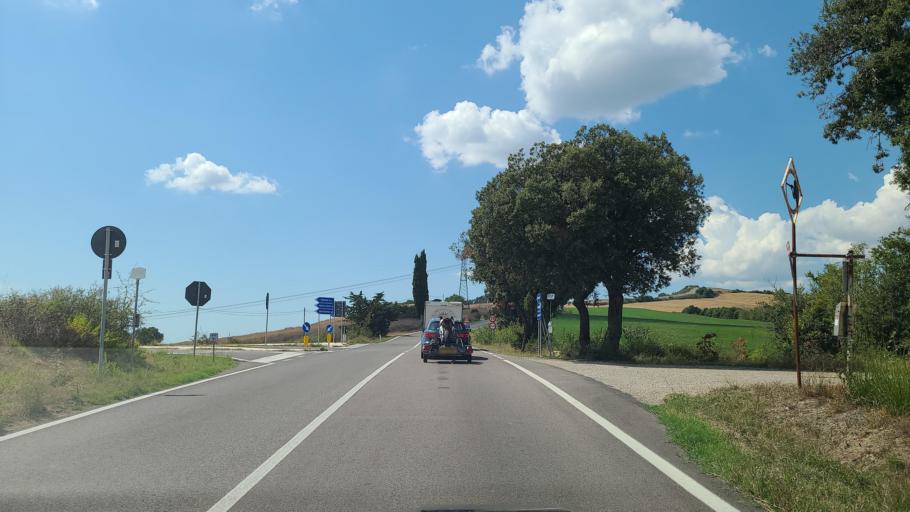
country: IT
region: Tuscany
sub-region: Provincia di Siena
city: San Gimignano
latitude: 43.4013
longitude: 10.9907
